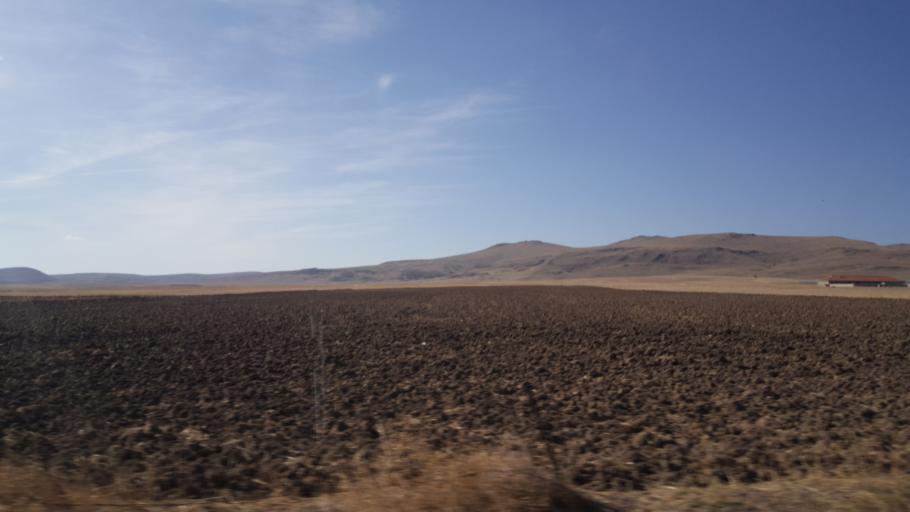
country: TR
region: Ankara
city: Altpinar
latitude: 39.2620
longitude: 32.7528
